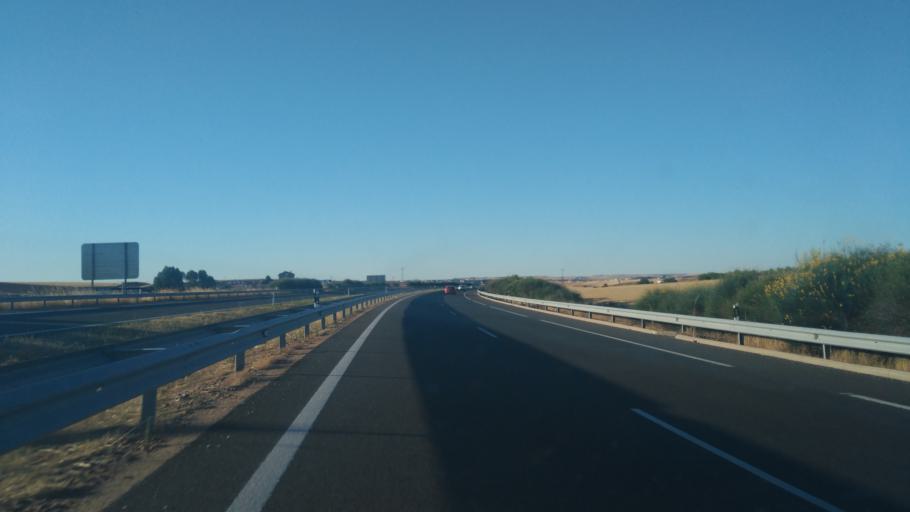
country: ES
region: Castille and Leon
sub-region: Provincia de Salamanca
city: Arapiles
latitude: 40.9034
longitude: -5.6625
